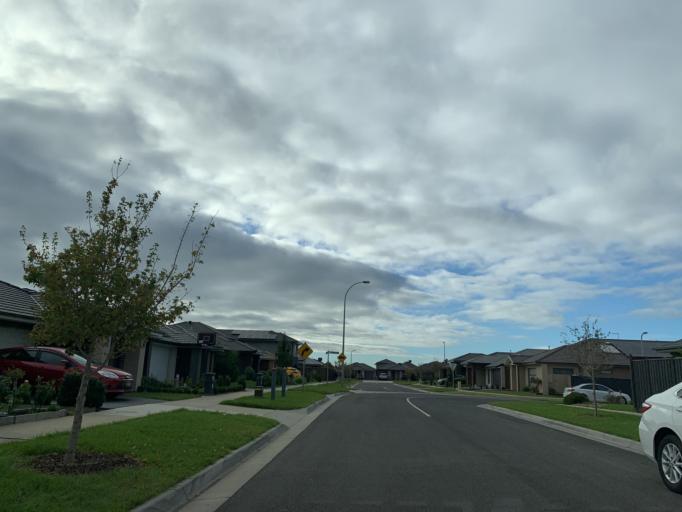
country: AU
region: Victoria
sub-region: Casey
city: Cranbourne East
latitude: -38.1233
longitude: 145.3395
